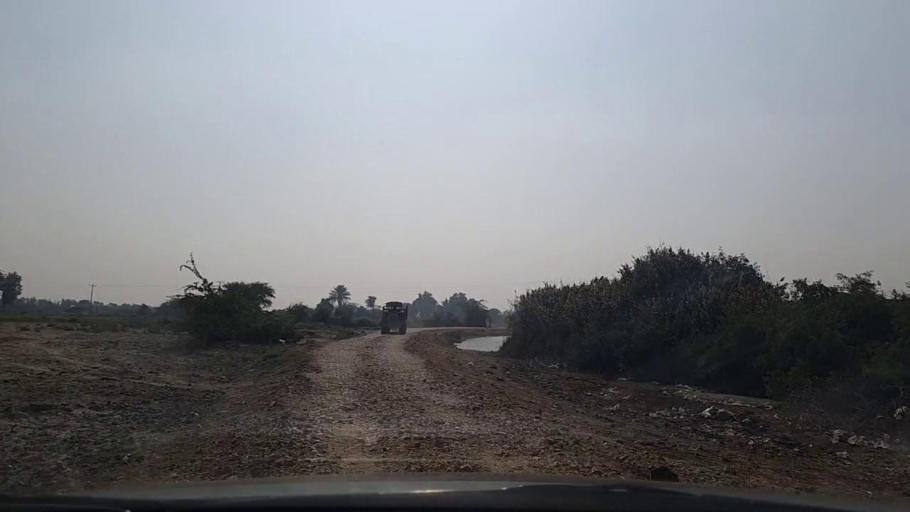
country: PK
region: Sindh
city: Mirpur Sakro
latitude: 24.5636
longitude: 67.7761
